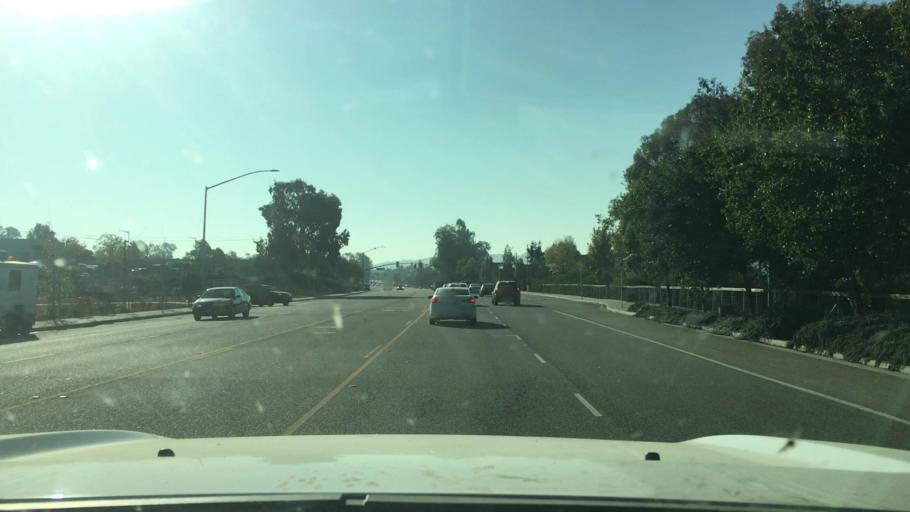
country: US
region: California
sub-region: San Luis Obispo County
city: San Luis Obispo
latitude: 35.2530
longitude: -120.6455
